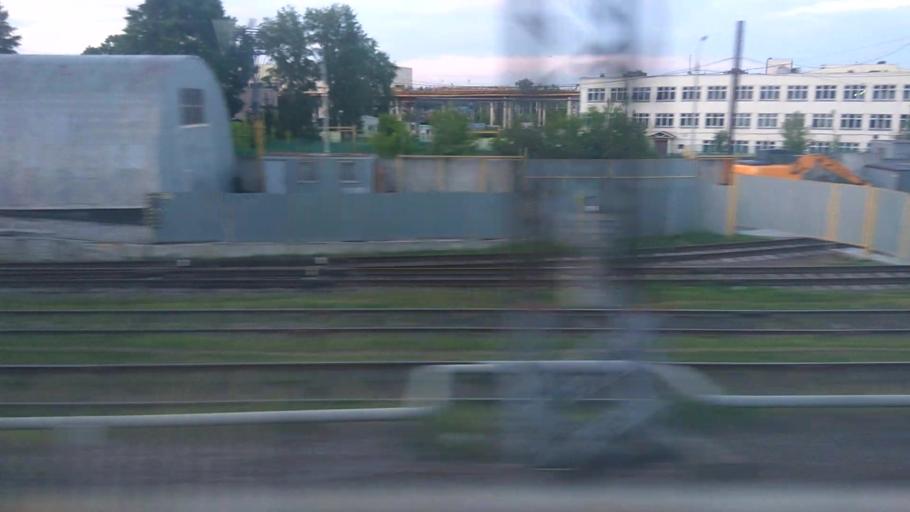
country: RU
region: Moskovskaya
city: Domodedovo
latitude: 55.4466
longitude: 37.7683
